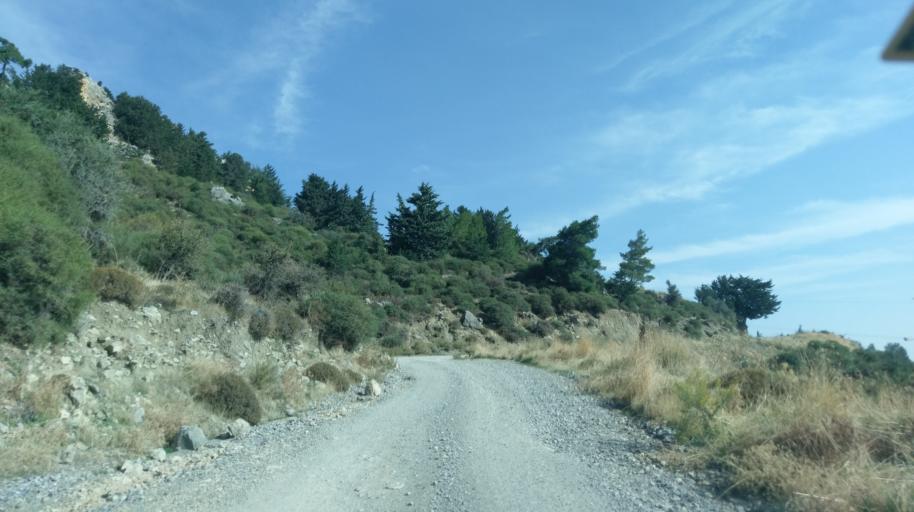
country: CY
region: Keryneia
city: Lapithos
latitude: 35.3077
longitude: 33.1928
